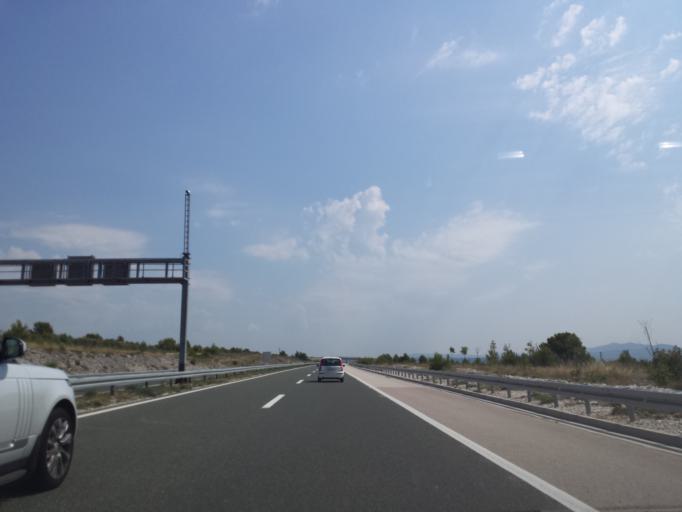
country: HR
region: Sibensko-Kniniska
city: Zaton
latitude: 43.8529
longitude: 15.8571
